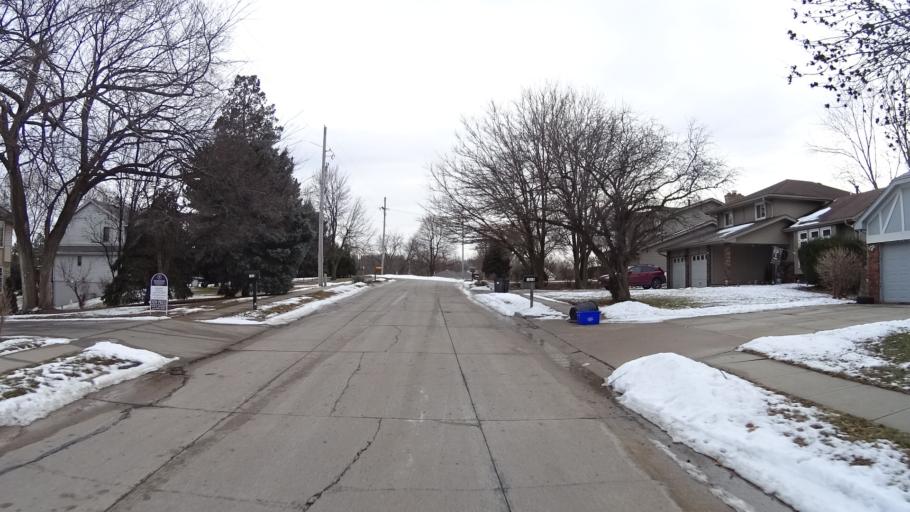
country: US
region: Nebraska
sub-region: Sarpy County
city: Bellevue
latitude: 41.1736
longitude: -95.9111
